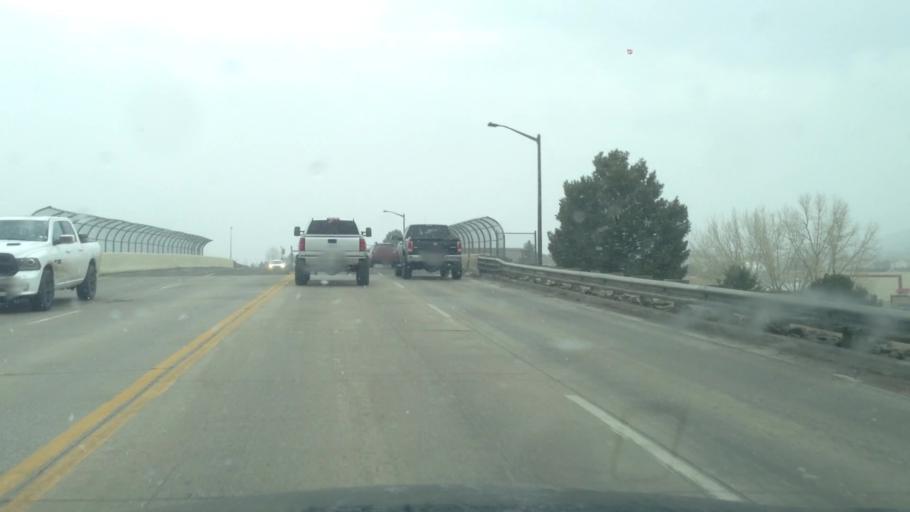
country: US
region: Colorado
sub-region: Douglas County
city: Castle Rock
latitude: 39.3641
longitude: -104.8596
